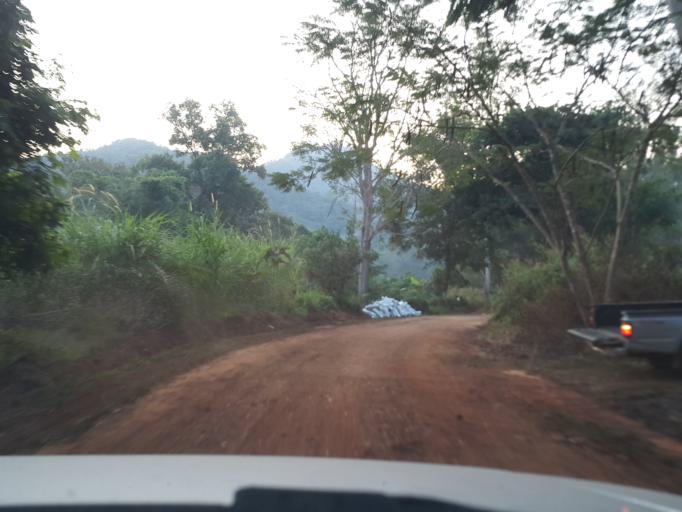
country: TH
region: Lamphun
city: Ban Thi
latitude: 18.5685
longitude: 99.2530
